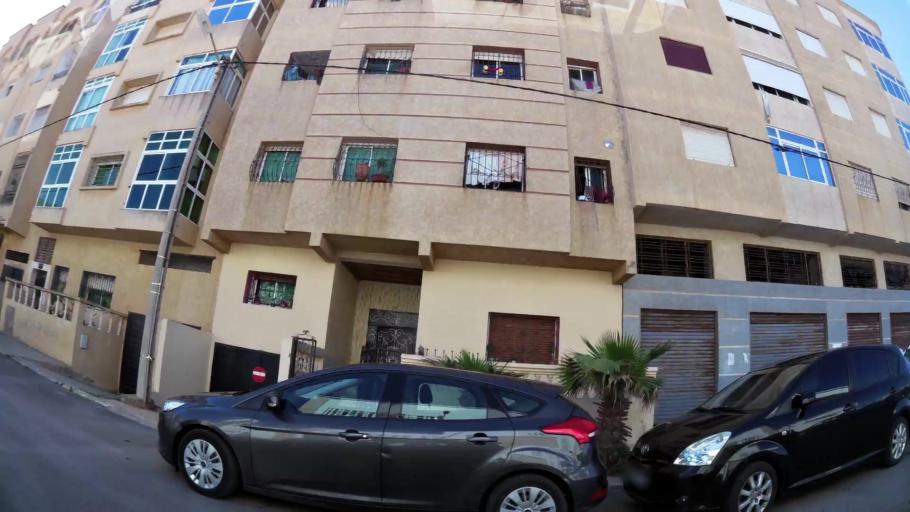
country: MA
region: Rabat-Sale-Zemmour-Zaer
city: Sale
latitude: 34.0678
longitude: -6.8022
